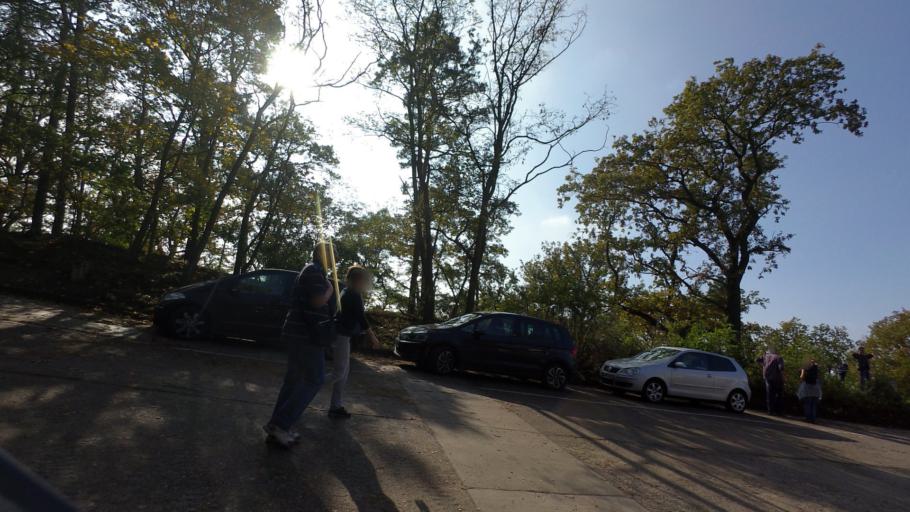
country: DE
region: Berlin
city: Friedrichshagen
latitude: 52.4168
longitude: 13.6267
